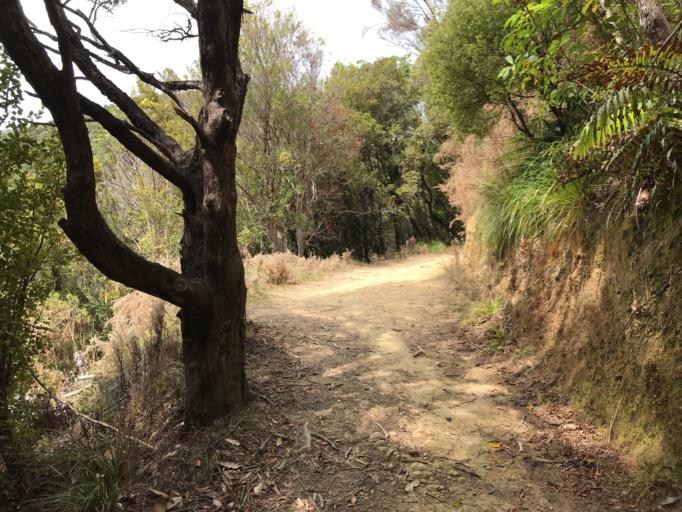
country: NZ
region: Marlborough
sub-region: Marlborough District
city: Picton
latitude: -41.1202
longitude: 174.2018
